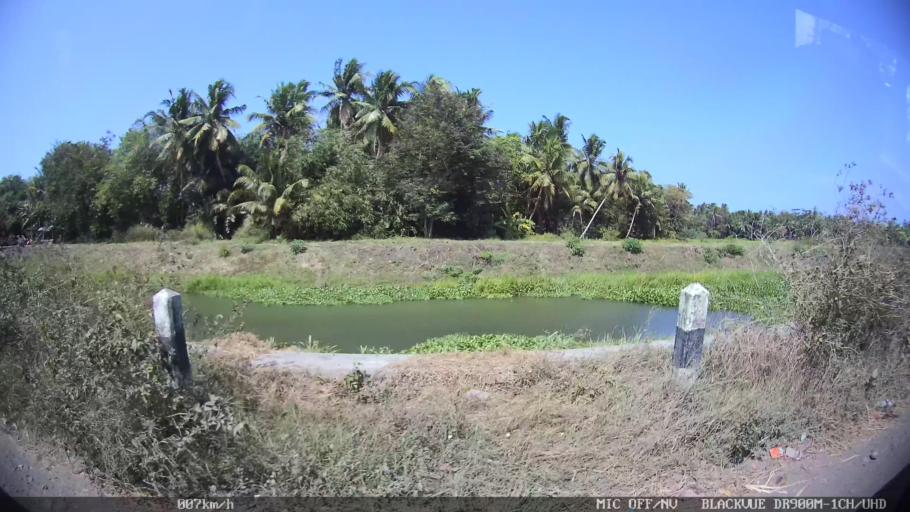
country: ID
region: Daerah Istimewa Yogyakarta
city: Srandakan
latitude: -7.9479
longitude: 110.1808
